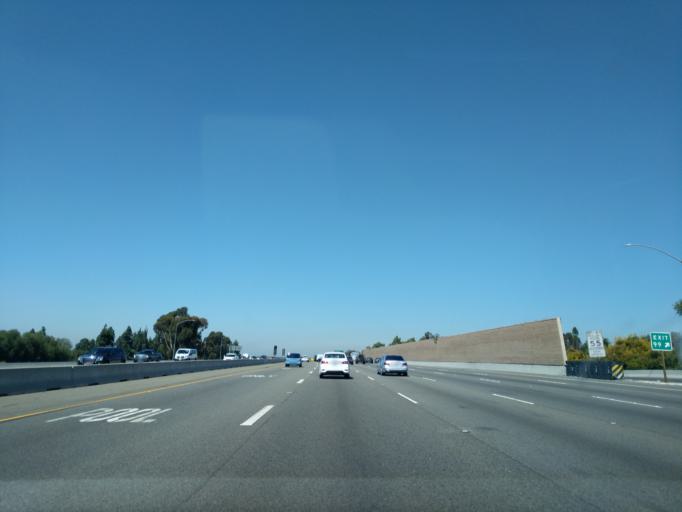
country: US
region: California
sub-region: Orange County
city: Irvine
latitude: 33.7077
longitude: -117.7800
